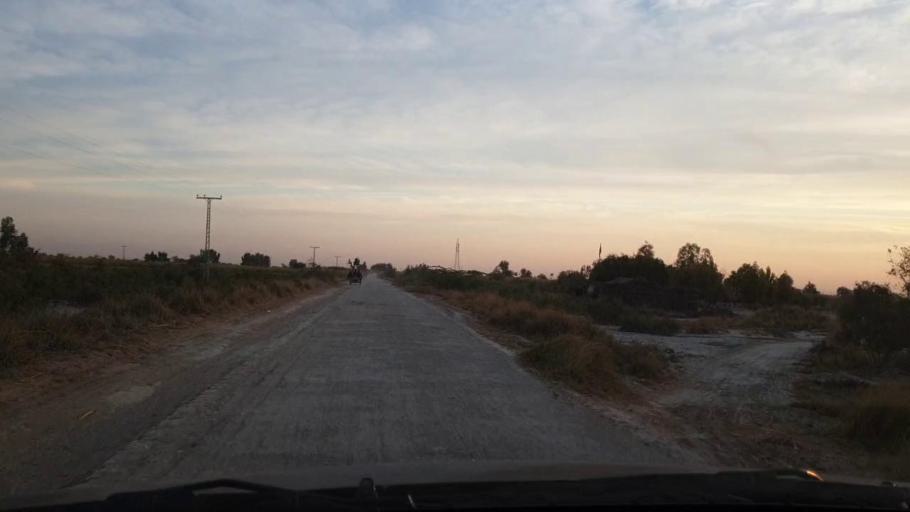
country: PK
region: Sindh
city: Khadro
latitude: 26.1169
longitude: 68.7962
